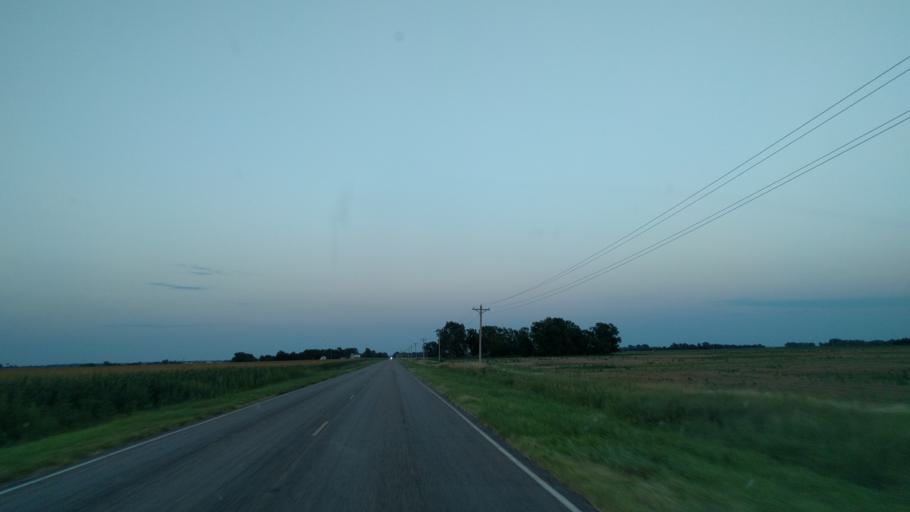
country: US
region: Kansas
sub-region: Rice County
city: Sterling
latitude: 38.2174
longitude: -98.1527
